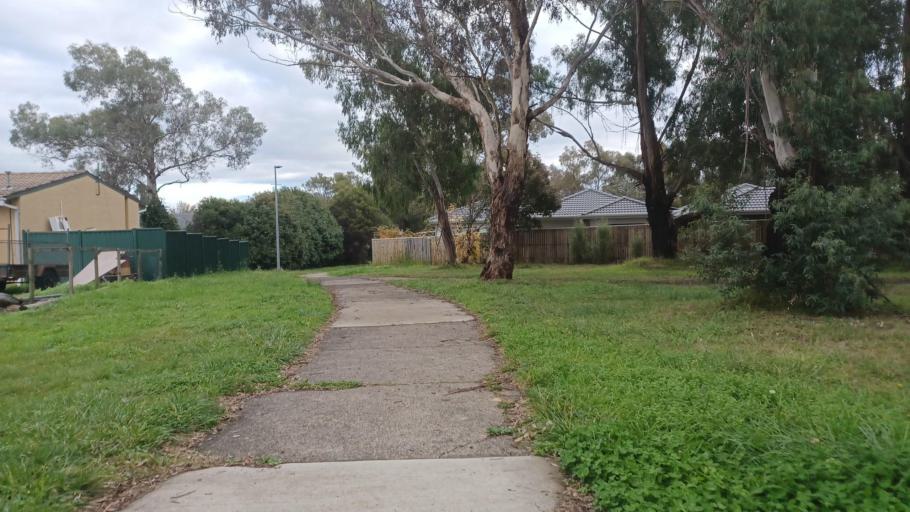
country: AU
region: Australian Capital Territory
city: Belconnen
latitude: -35.2008
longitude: 149.0409
